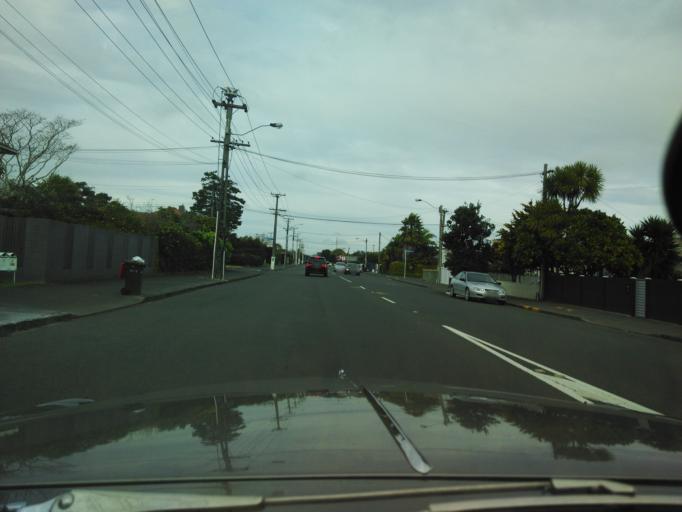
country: NZ
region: Auckland
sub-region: Auckland
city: Rosebank
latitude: -36.8615
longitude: 174.7035
